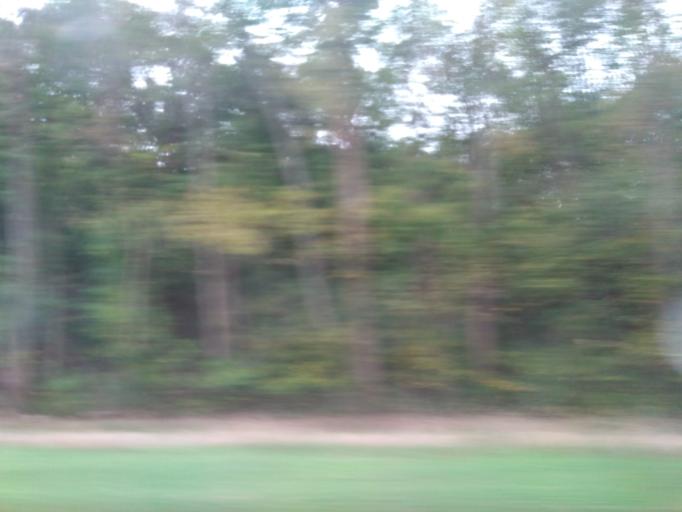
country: US
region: Illinois
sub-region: Bond County
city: Greenville
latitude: 38.8334
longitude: -89.5236
